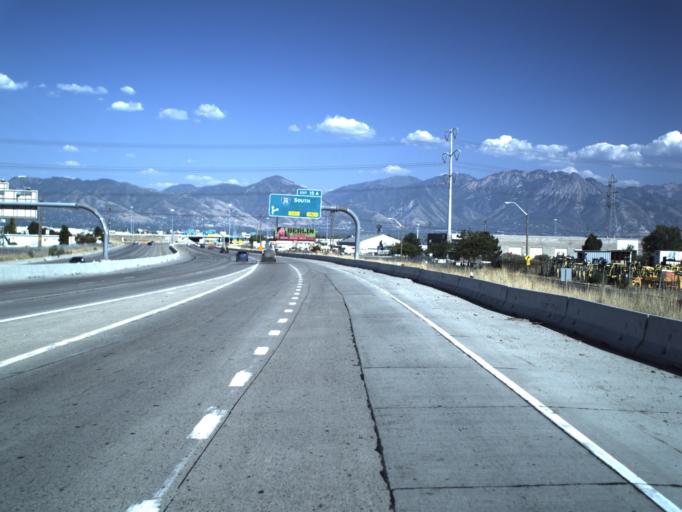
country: US
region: Utah
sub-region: Salt Lake County
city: West Valley City
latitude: 40.7258
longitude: -111.9625
